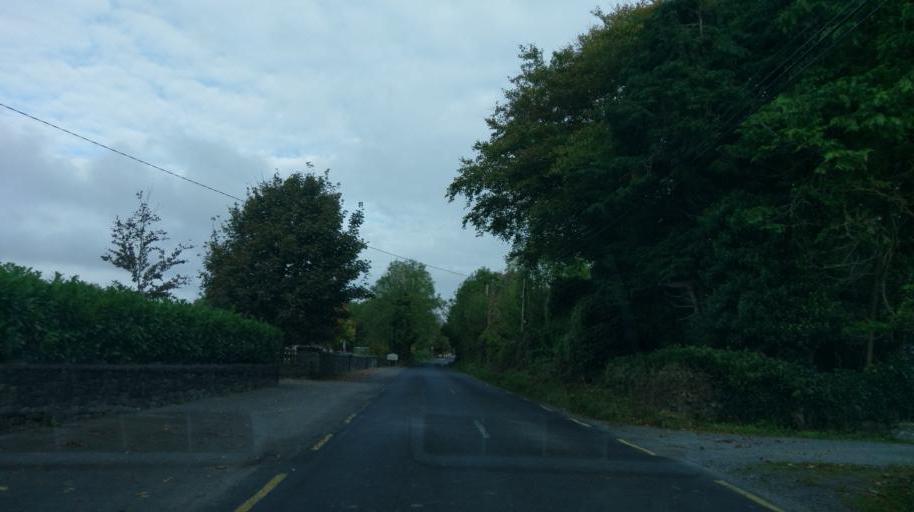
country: IE
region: Connaught
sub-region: County Galway
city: Athenry
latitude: 53.3683
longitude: -8.7006
